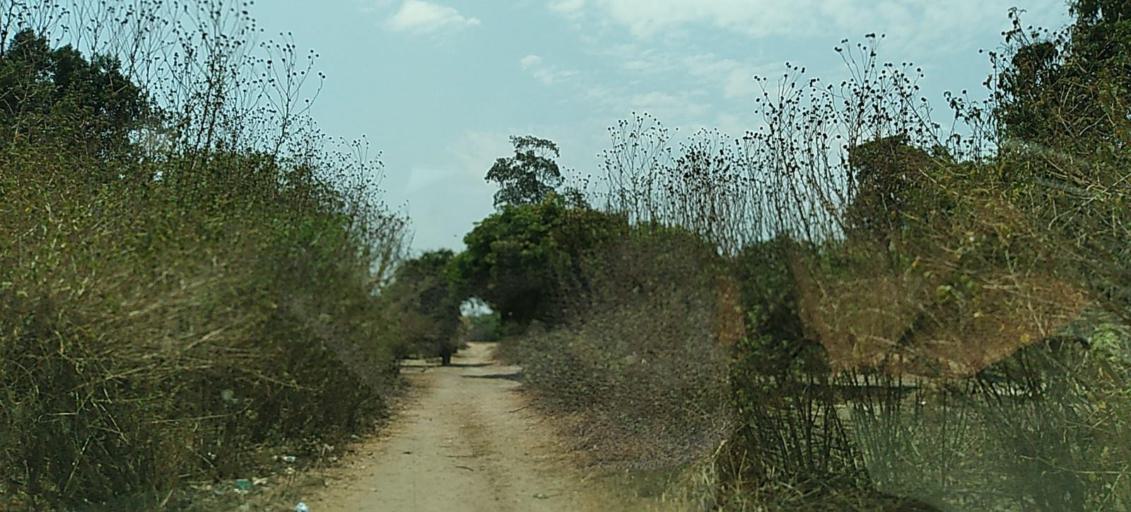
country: ZM
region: Copperbelt
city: Kalulushi
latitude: -12.9536
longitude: 28.1409
